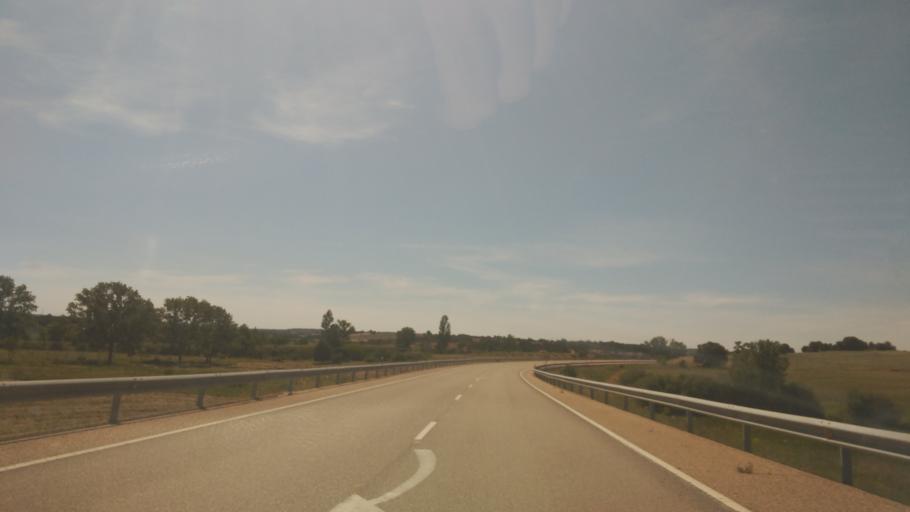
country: ES
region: Castille and Leon
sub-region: Provincia de Zamora
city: Cuelgamures
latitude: 41.2591
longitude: -5.7078
